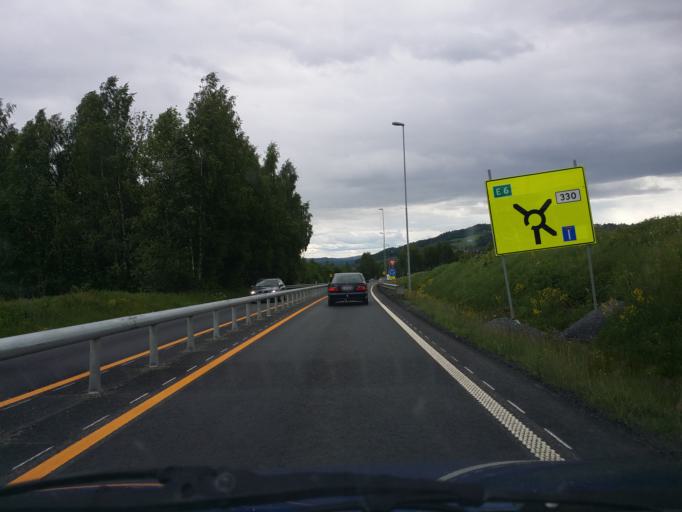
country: NO
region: Hedmark
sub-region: Ringsaker
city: Moelv
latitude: 60.9731
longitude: 10.5927
